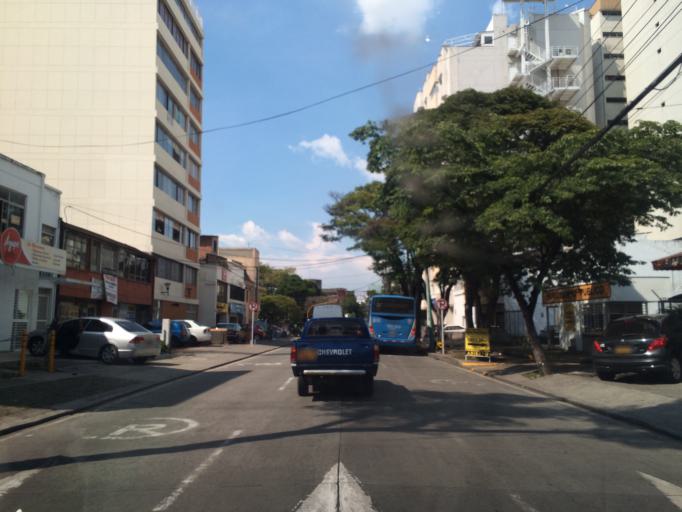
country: CO
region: Valle del Cauca
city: Cali
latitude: 3.4630
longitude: -76.5270
